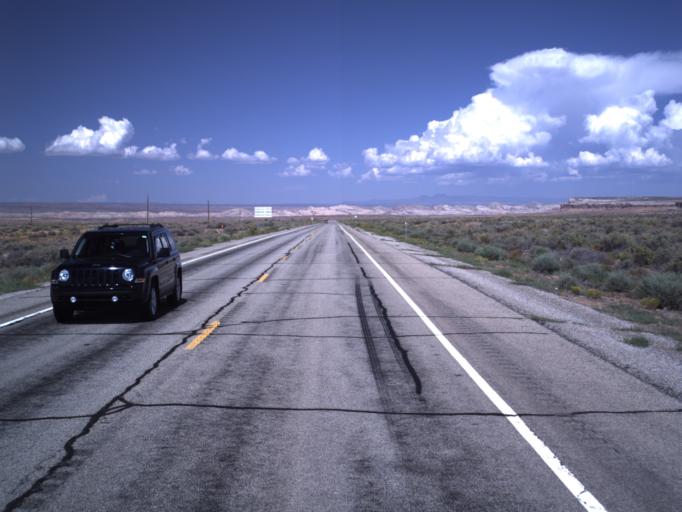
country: US
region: Utah
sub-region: San Juan County
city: Blanding
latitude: 37.1838
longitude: -109.5905
